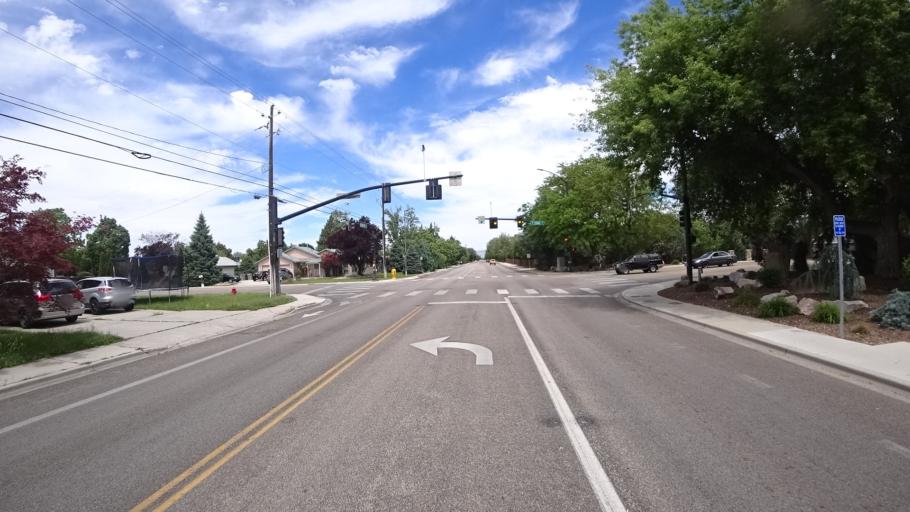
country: US
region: Idaho
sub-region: Ada County
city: Eagle
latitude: 43.6409
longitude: -116.3142
